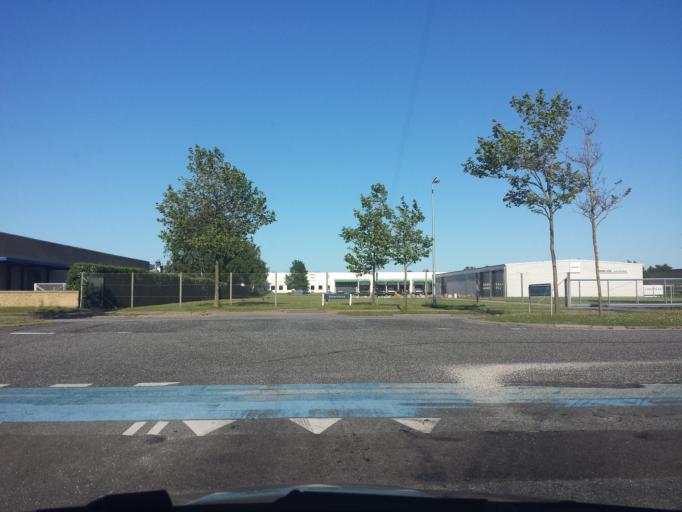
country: DK
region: Capital Region
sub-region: Glostrup Kommune
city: Glostrup
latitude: 55.6794
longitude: 12.3898
